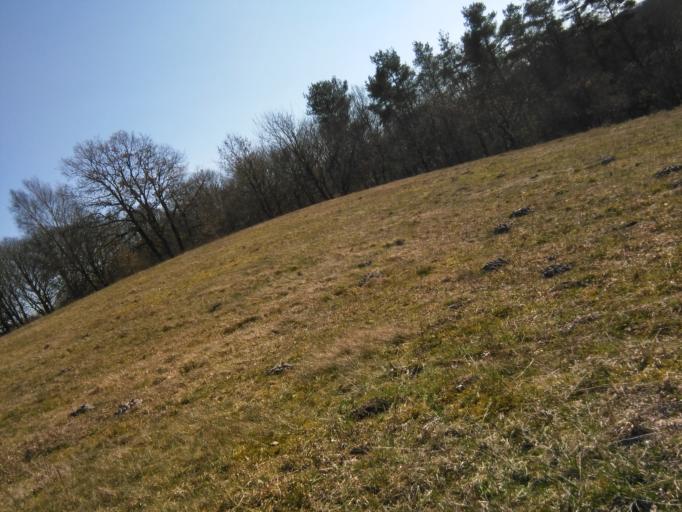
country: DK
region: Central Jutland
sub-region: Hedensted Kommune
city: Torring
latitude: 55.9131
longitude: 9.3997
